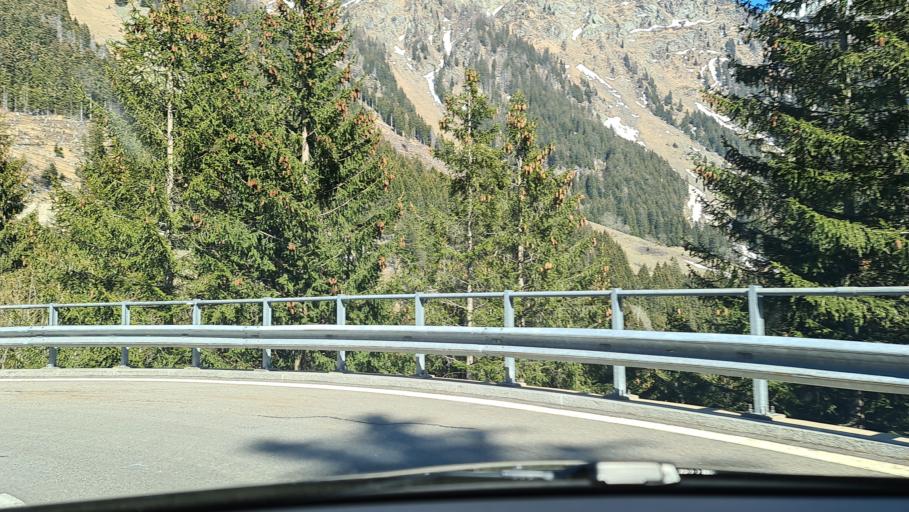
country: CH
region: Grisons
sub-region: Moesa District
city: Mesocco
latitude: 46.4356
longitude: 9.2119
